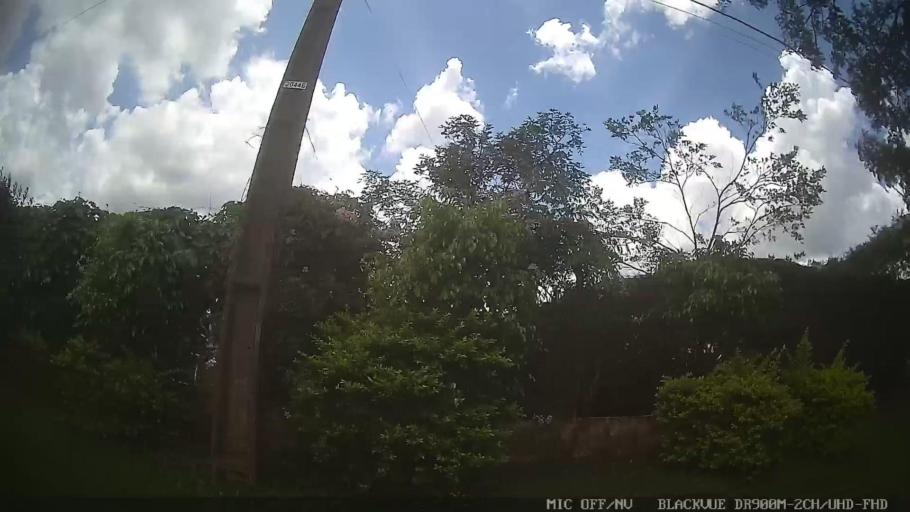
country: BR
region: Sao Paulo
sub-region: Braganca Paulista
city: Braganca Paulista
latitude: -23.0342
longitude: -46.5290
